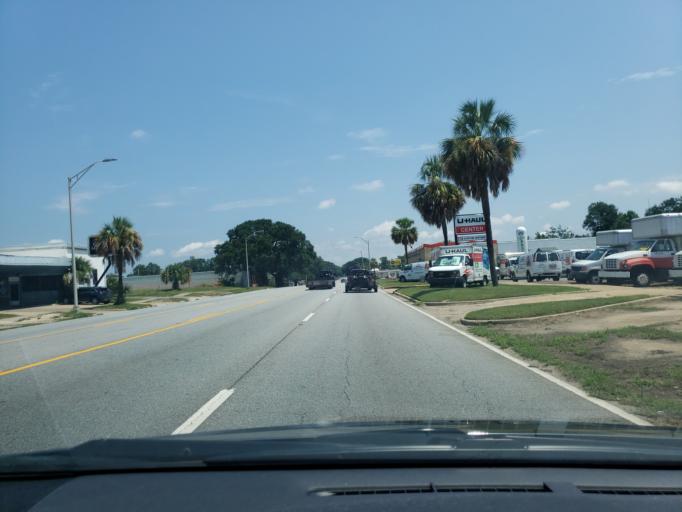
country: US
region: Georgia
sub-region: Dougherty County
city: Albany
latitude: 31.5752
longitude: -84.1694
